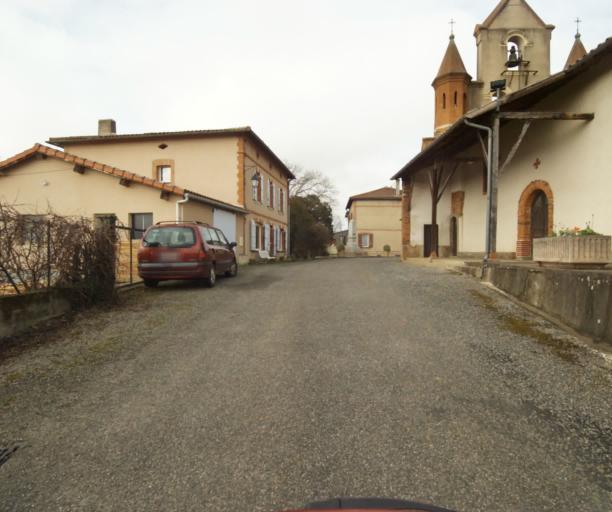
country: FR
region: Midi-Pyrenees
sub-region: Departement de l'Ariege
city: Pamiers
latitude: 43.1056
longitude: 1.5155
